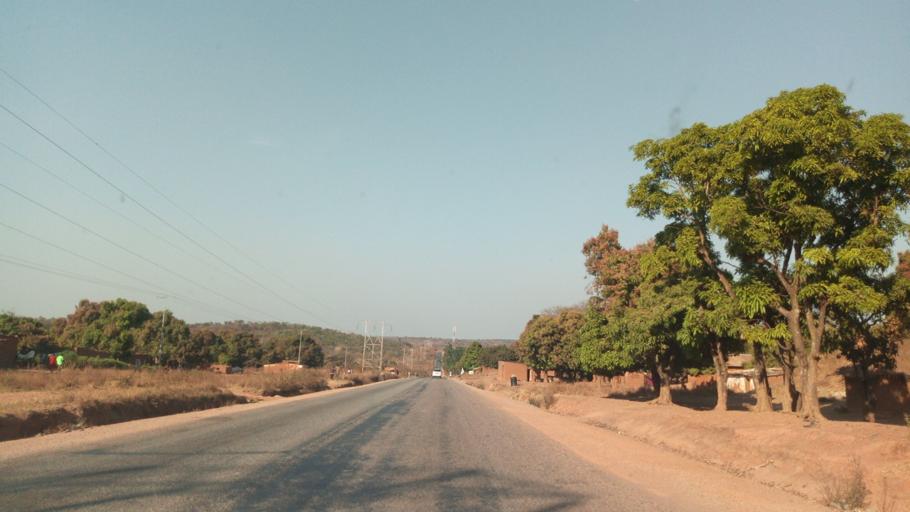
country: CD
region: Katanga
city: Likasi
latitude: -11.0007
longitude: 26.8814
